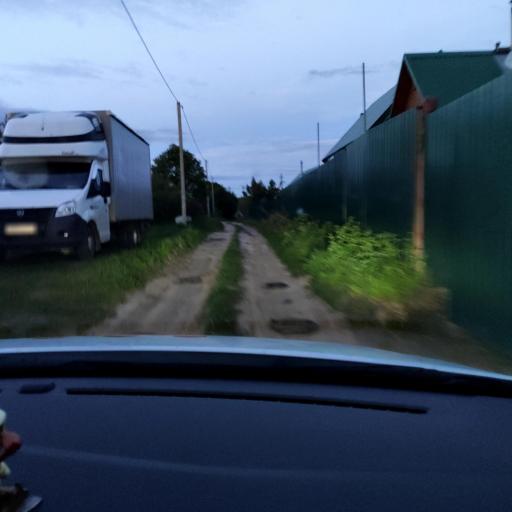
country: RU
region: Tatarstan
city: Stolbishchi
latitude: 55.5951
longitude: 49.0963
